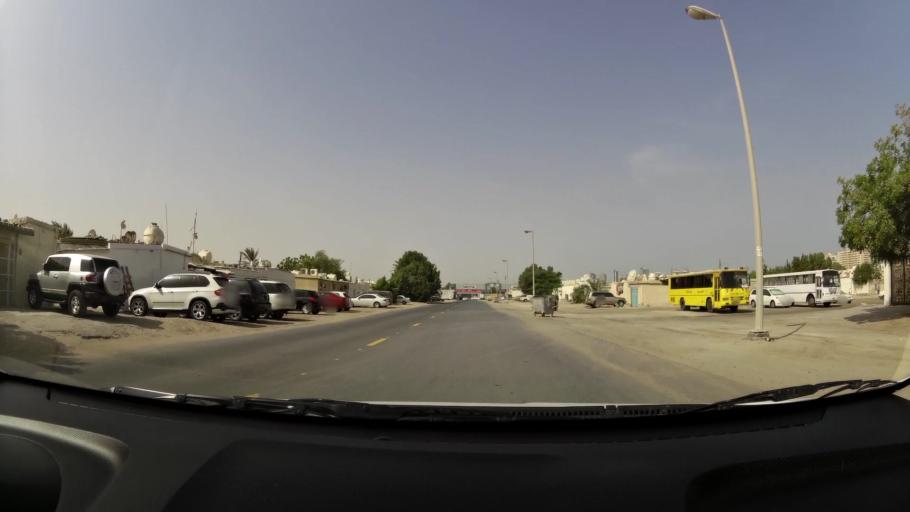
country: AE
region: Ash Shariqah
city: Sharjah
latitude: 25.3429
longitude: 55.4112
